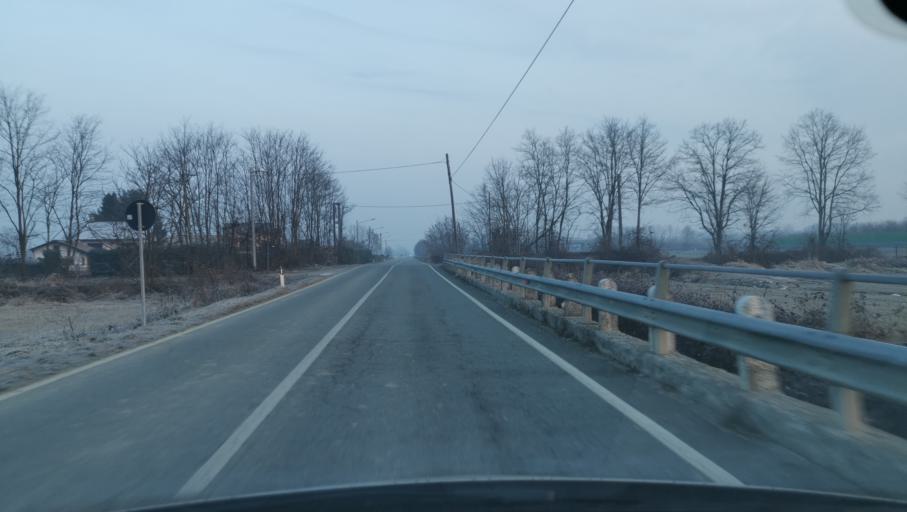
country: IT
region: Piedmont
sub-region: Provincia di Torino
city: Foglizzo
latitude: 45.2708
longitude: 7.8116
